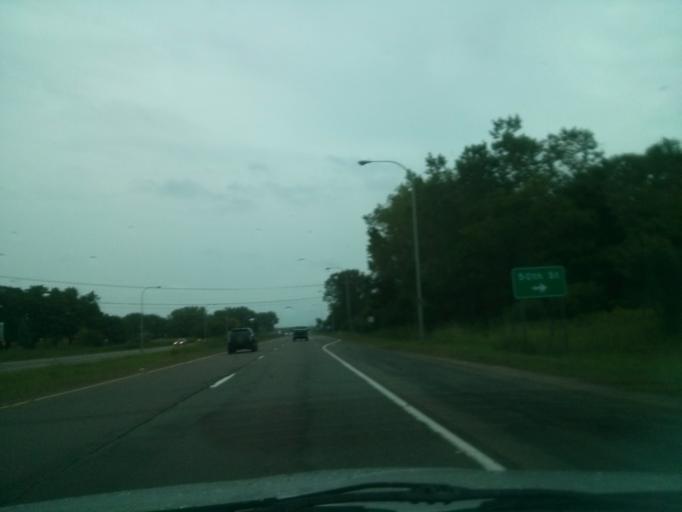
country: US
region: Minnesota
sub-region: Ramsey County
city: North Saint Paul
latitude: 45.0205
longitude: -92.9835
